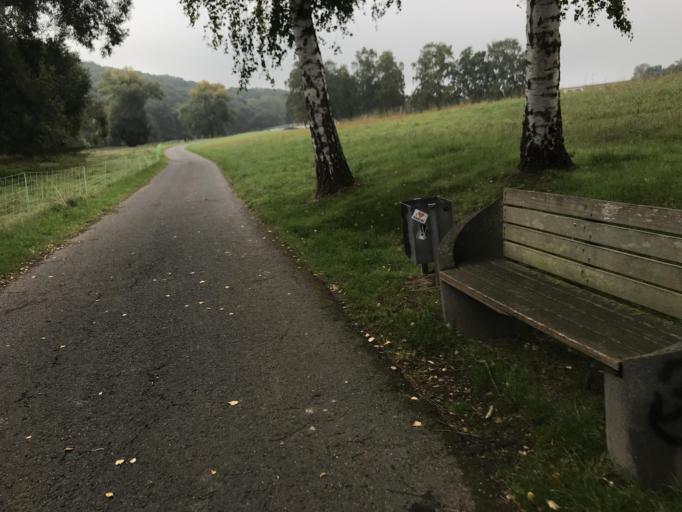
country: DE
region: Hesse
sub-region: Regierungsbezirk Kassel
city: Guxhagen
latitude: 51.2311
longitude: 9.4731
